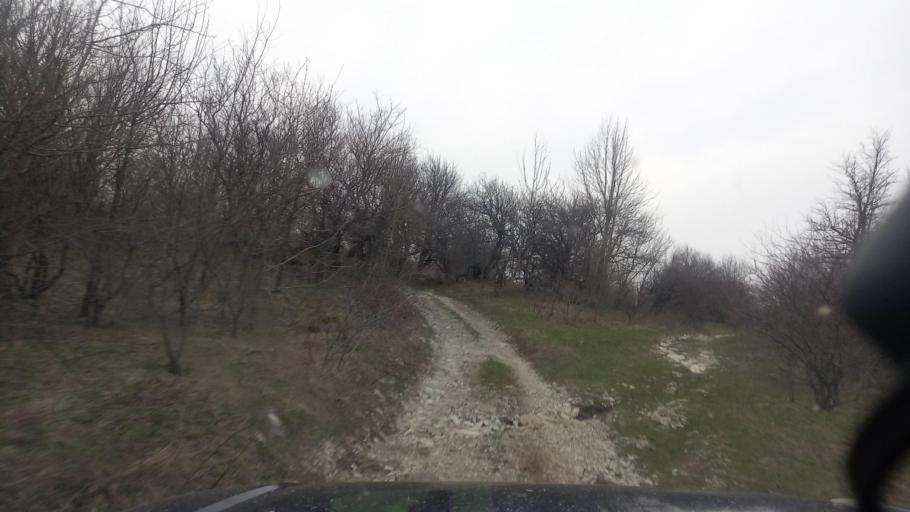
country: RU
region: Krasnodarskiy
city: Pshada
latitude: 44.5993
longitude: 38.2809
